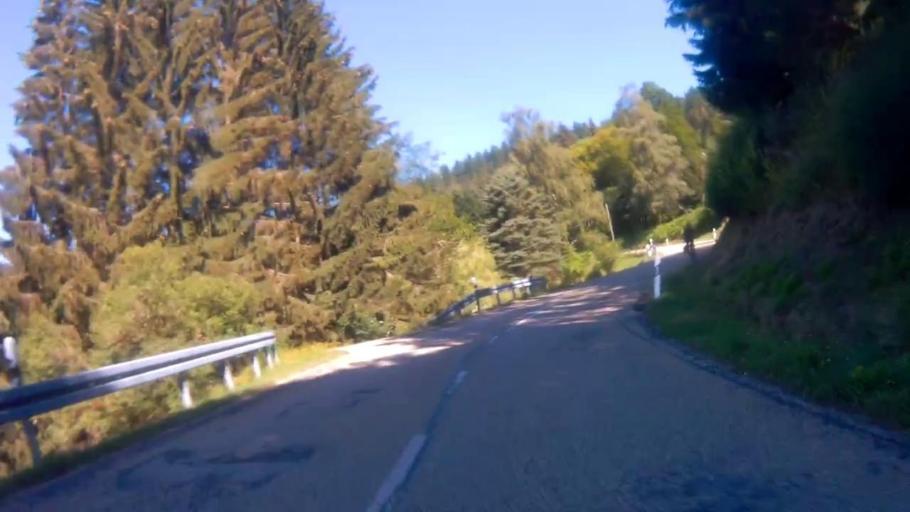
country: DE
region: Baden-Wuerttemberg
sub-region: Freiburg Region
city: Sulzburg
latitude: 47.7681
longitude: 7.7519
